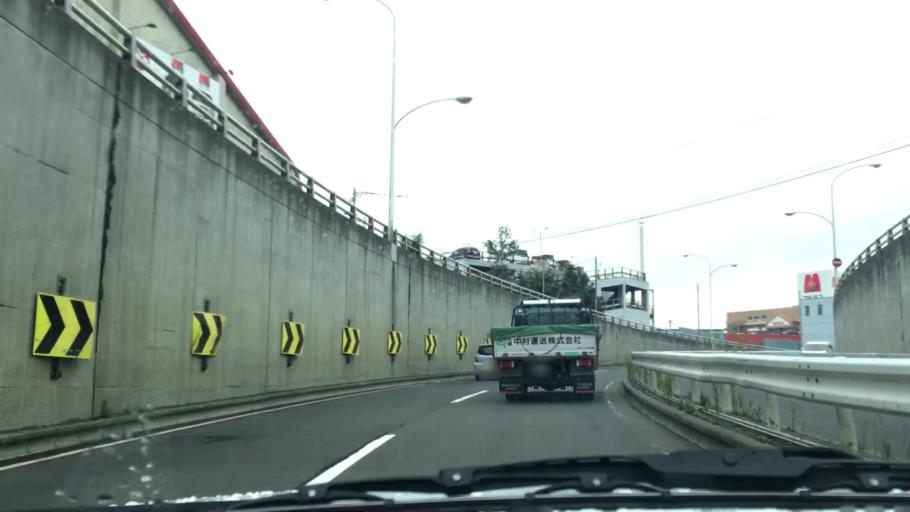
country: JP
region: Hokkaido
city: Sapporo
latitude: 43.0686
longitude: 141.3811
